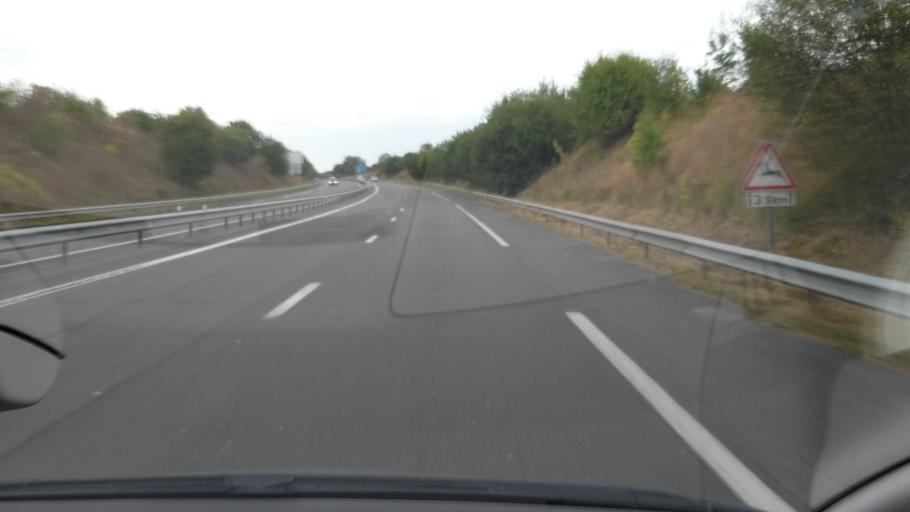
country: FR
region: Champagne-Ardenne
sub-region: Departement des Ardennes
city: La Francheville
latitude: 49.6493
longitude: 4.6326
